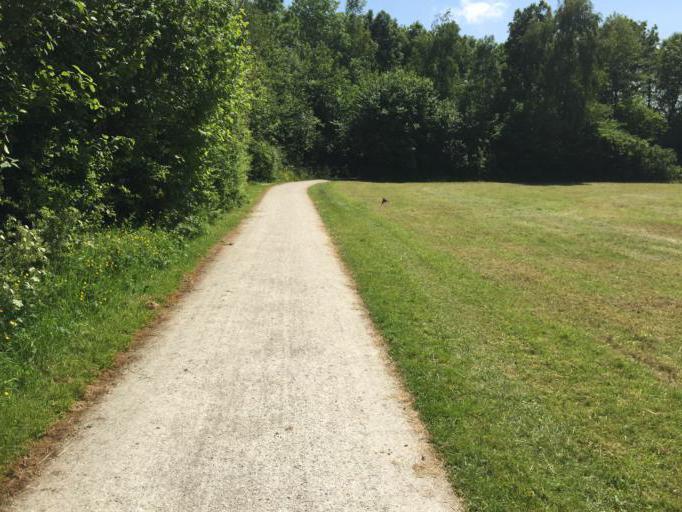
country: NL
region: Groningen
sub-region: Gemeente Zuidhorn
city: Grijpskerk
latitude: 53.2161
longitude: 6.3373
